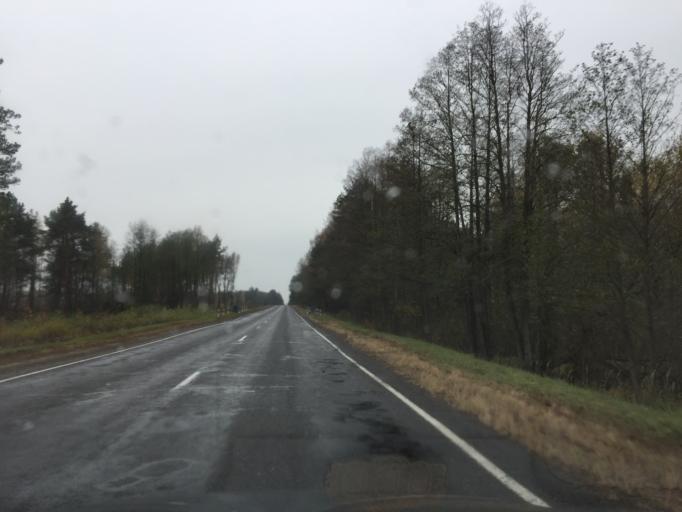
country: BY
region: Gomel
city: Karma
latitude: 53.3314
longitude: 30.7838
